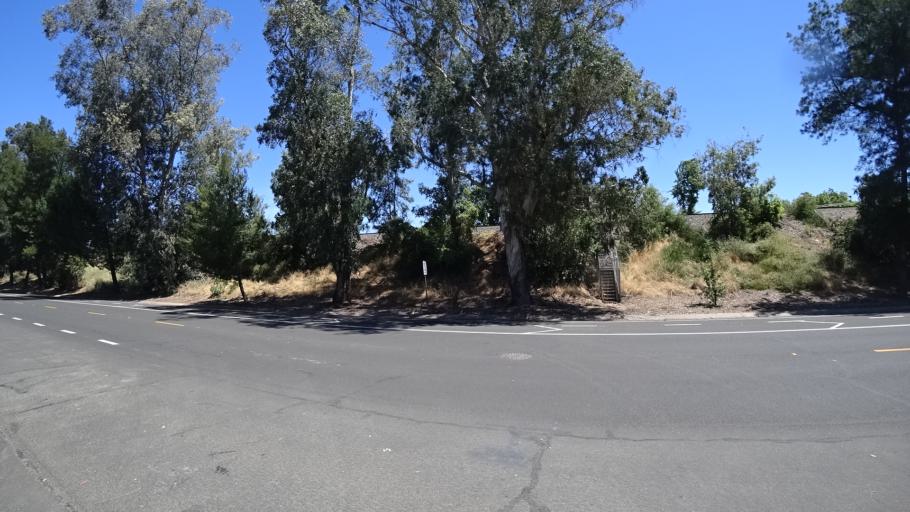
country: US
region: California
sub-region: Sacramento County
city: Sacramento
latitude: 38.5768
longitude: -121.4356
